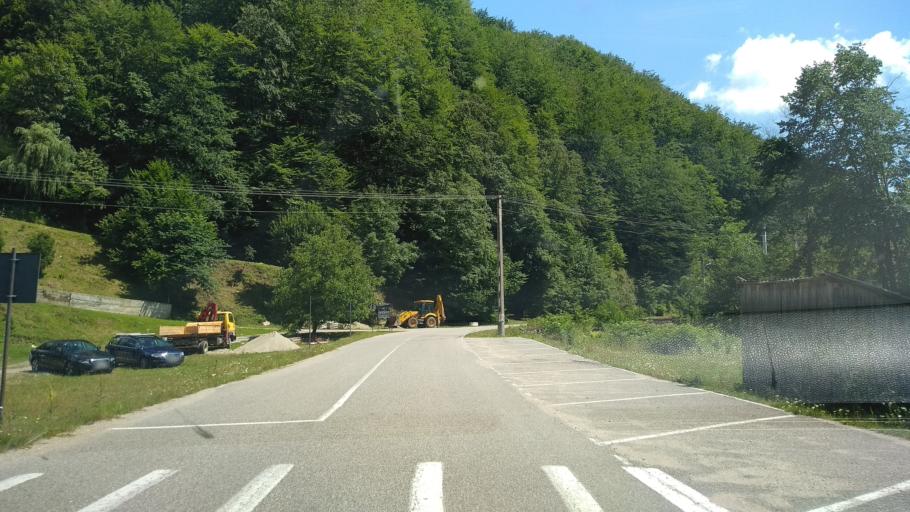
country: RO
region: Hunedoara
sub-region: Comuna Orastioara de Sus
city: Orastioara de Sus
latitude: 45.6323
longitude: 23.2151
